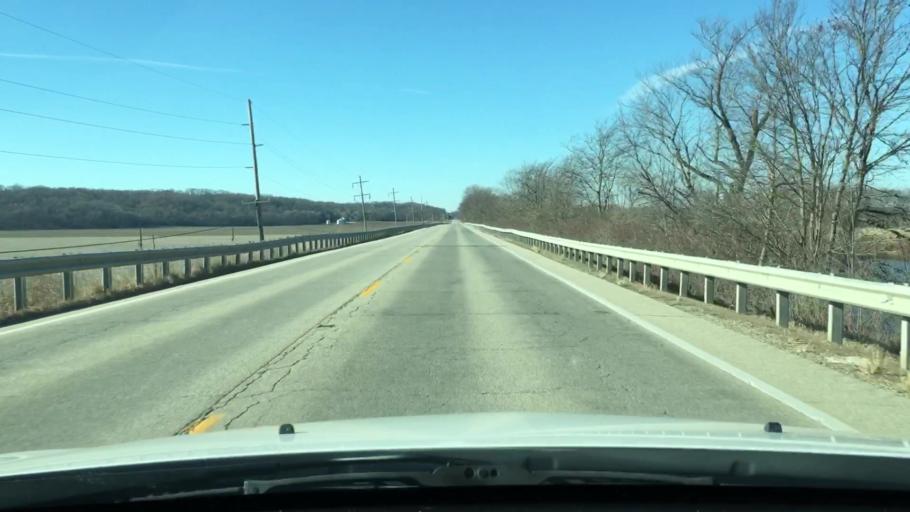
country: US
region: Illinois
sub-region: Mason County
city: Havana
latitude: 40.3018
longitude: -90.1184
